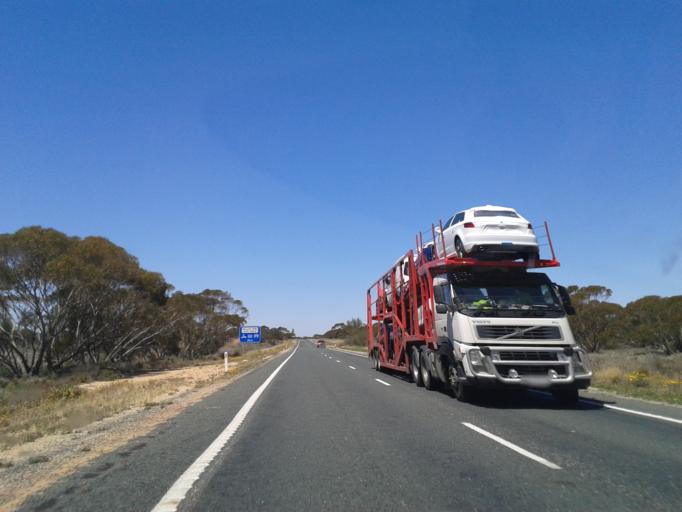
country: AU
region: New South Wales
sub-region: Wentworth
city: Gol Gol
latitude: -34.3729
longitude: 142.4160
